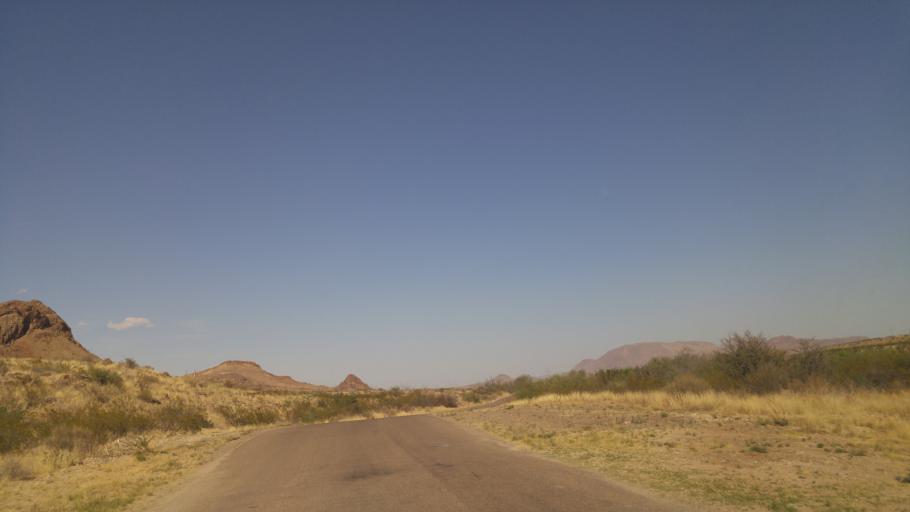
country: US
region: Texas
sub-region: Brewster County
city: Alpine
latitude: 29.5307
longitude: -103.4209
